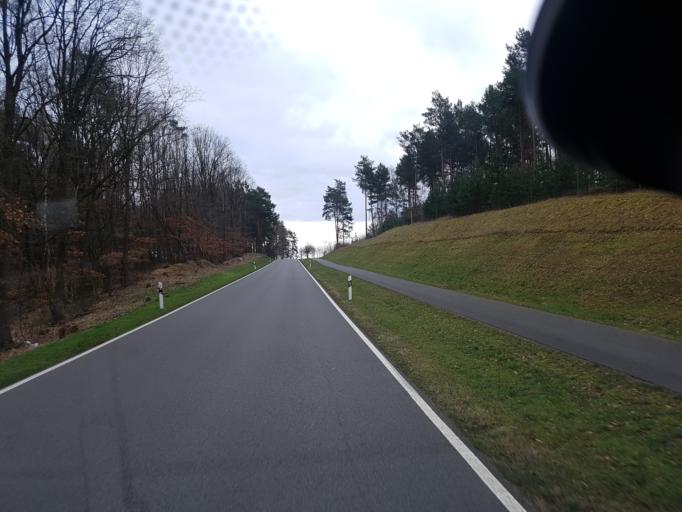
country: DE
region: Brandenburg
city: Gross Lindow
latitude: 52.1582
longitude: 14.5129
